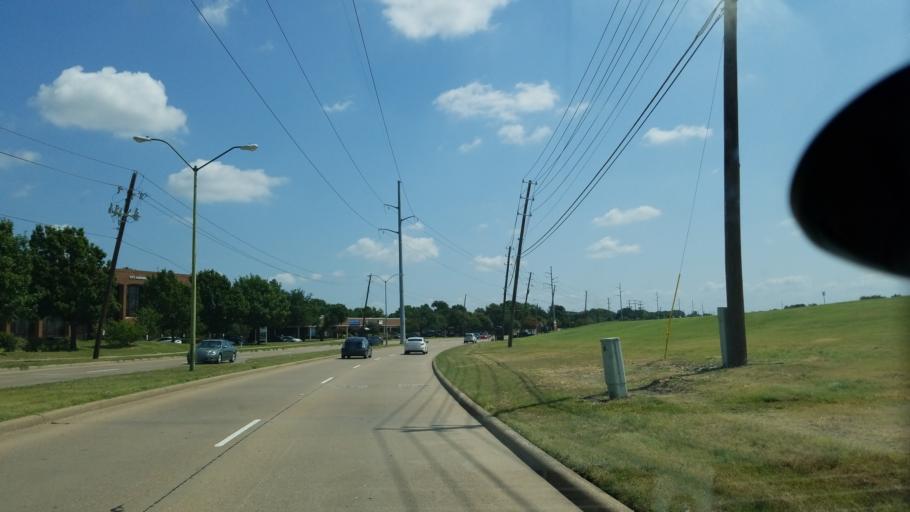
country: US
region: Texas
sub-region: Dallas County
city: Richardson
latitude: 32.9248
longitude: -96.7341
